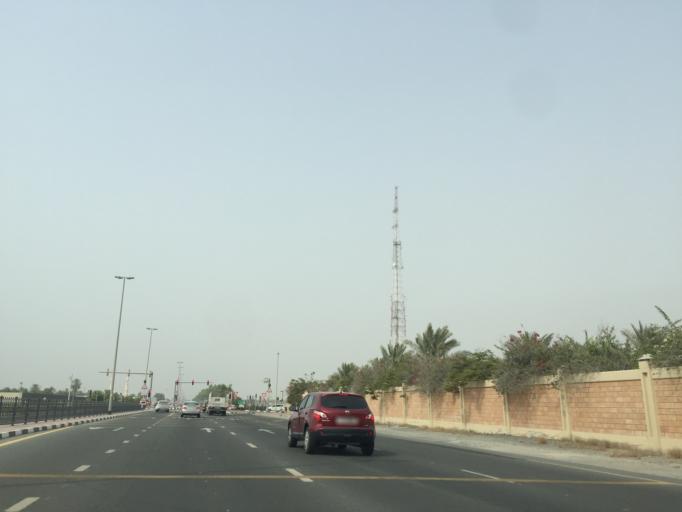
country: AE
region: Dubai
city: Dubai
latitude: 25.1180
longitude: 55.1798
